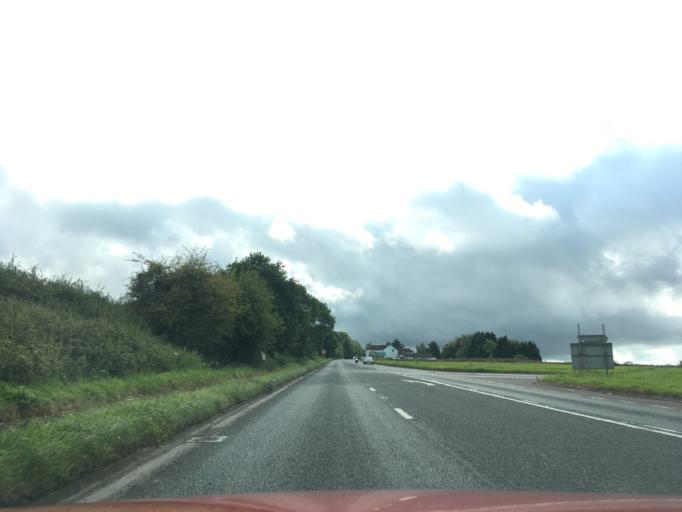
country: GB
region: England
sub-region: South Gloucestershire
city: Tytherington
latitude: 51.6127
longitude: -2.4844
